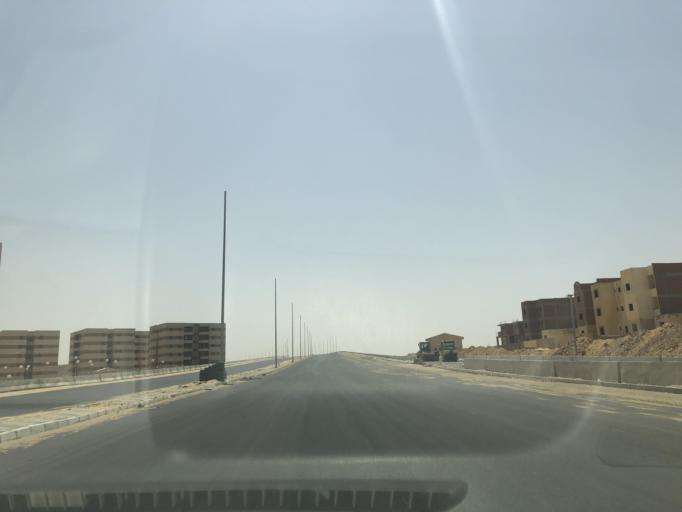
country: EG
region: Al Jizah
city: Madinat Sittah Uktubar
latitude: 29.9198
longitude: 31.0233
